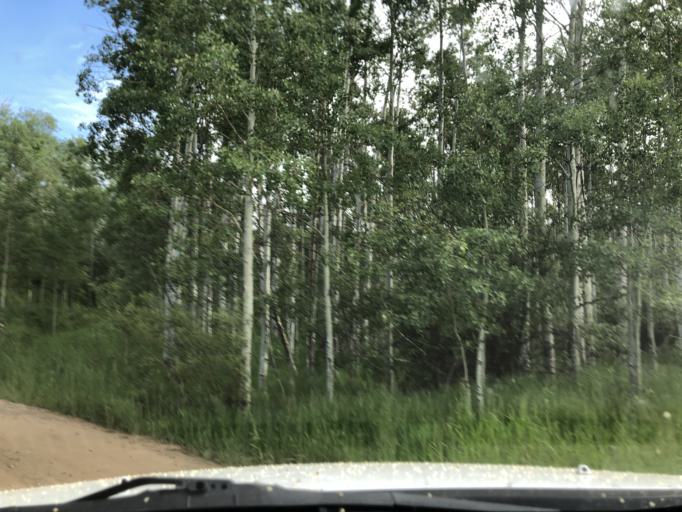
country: US
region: Colorado
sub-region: Delta County
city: Paonia
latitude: 39.0347
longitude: -107.3356
